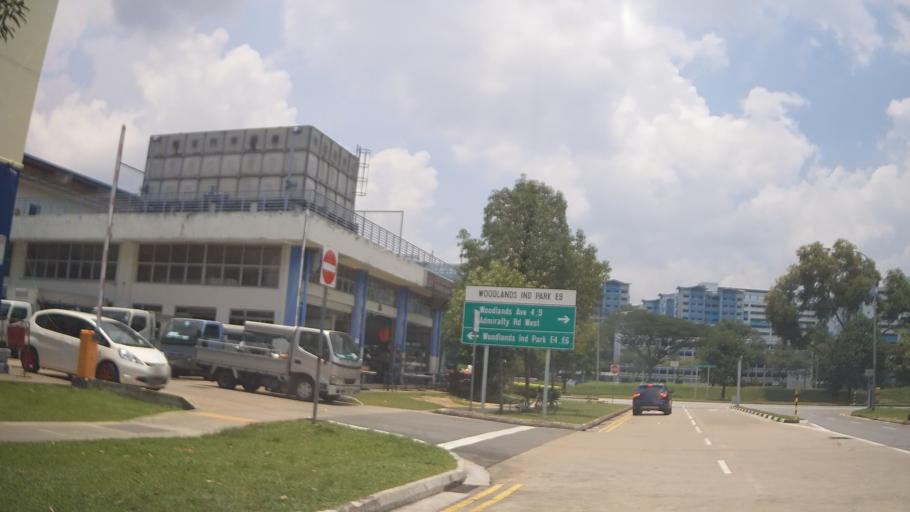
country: MY
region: Johor
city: Johor Bahru
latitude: 1.4485
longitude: 103.7932
